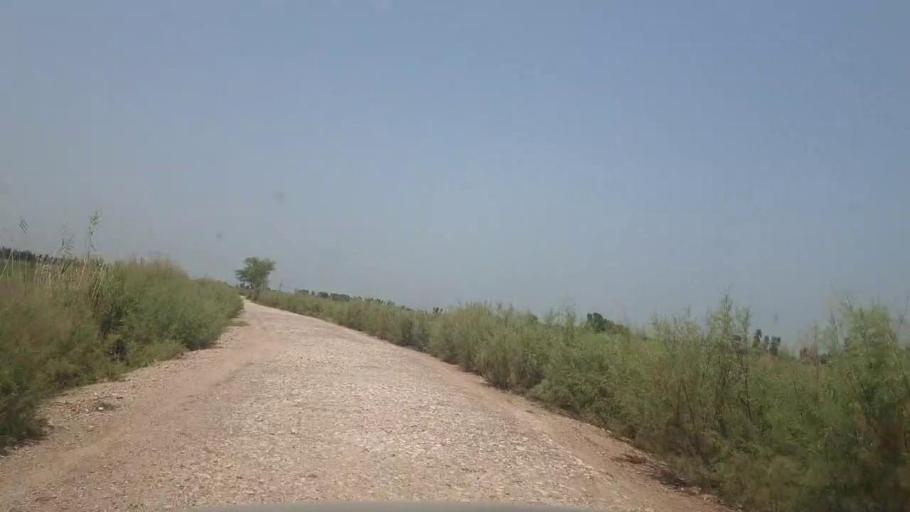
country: PK
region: Sindh
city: Lakhi
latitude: 27.8494
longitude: 68.6246
